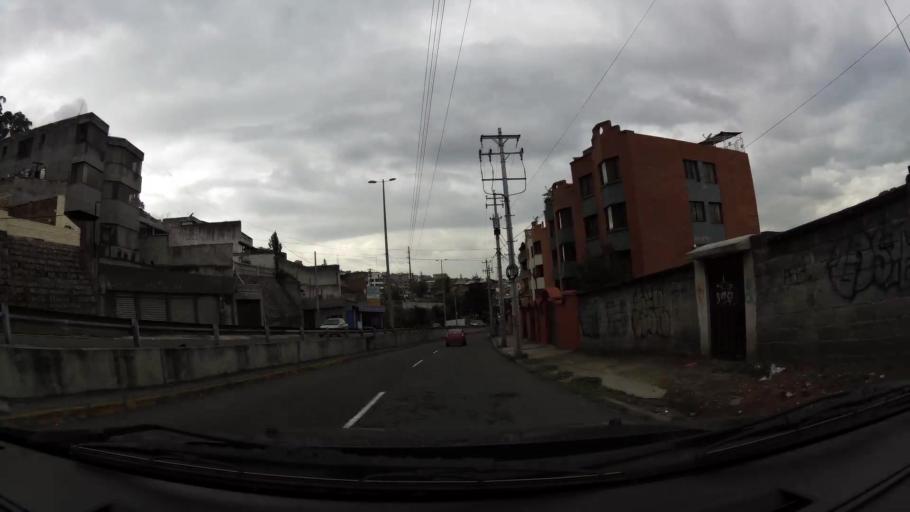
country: EC
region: Pichincha
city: Quito
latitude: -0.1953
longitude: -78.5119
